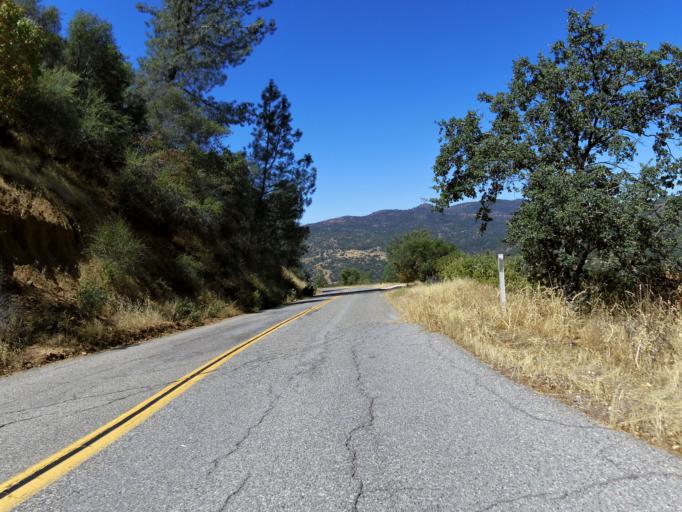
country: US
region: California
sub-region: Fresno County
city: Auberry
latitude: 37.1788
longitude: -119.5141
